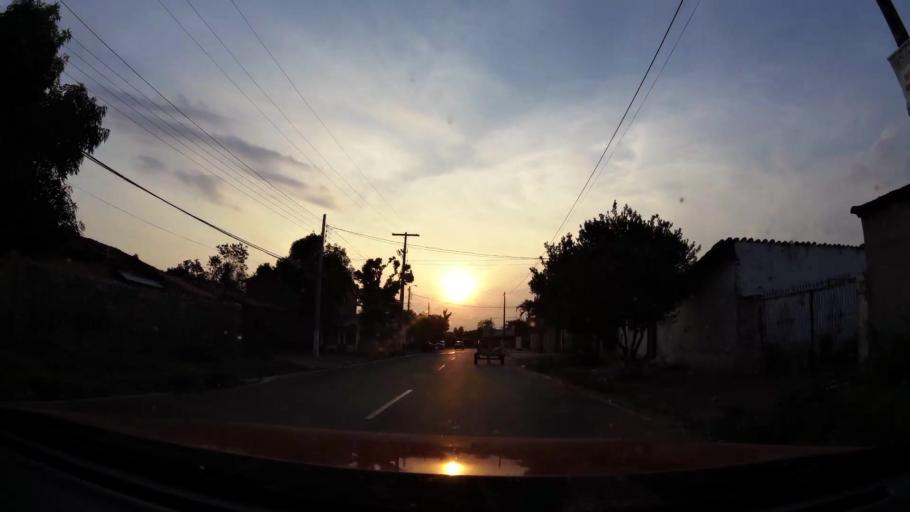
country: PY
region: Central
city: Lambare
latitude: -25.3575
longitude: -57.6065
